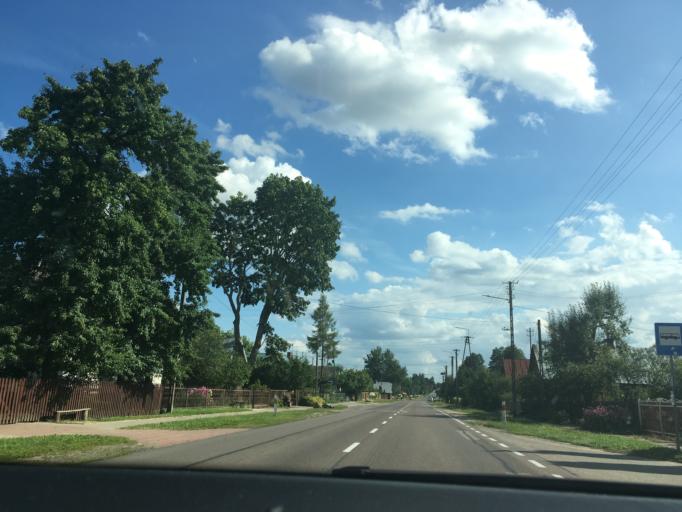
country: PL
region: Podlasie
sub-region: Powiat bialostocki
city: Zabludow
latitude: 52.9336
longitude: 23.2638
